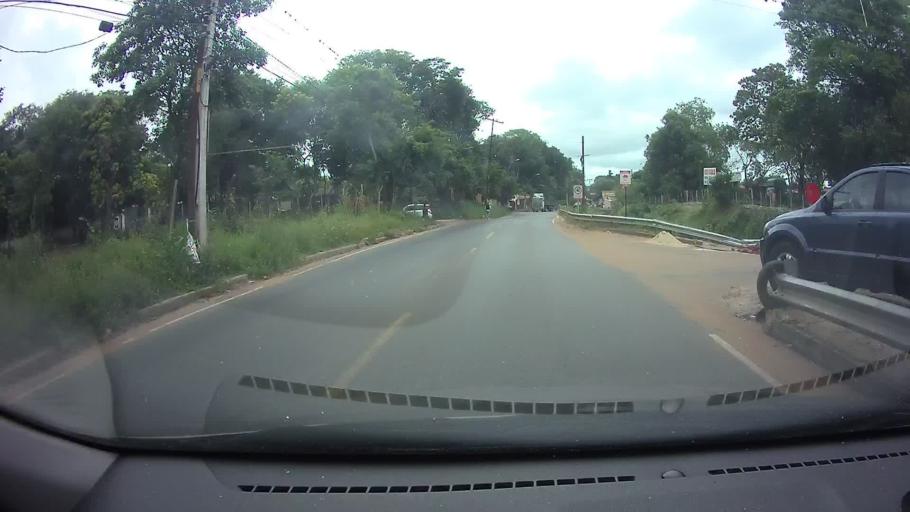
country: PY
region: Central
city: Nemby
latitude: -25.3783
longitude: -57.5455
